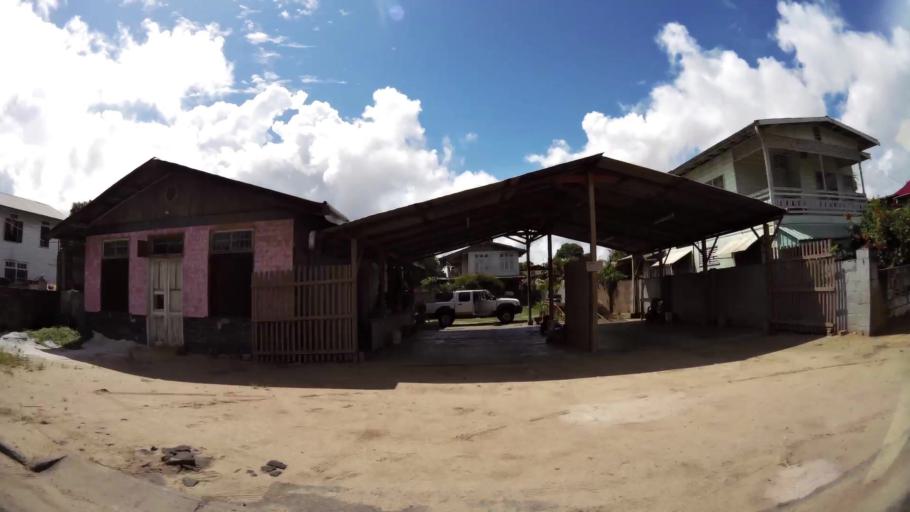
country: SR
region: Paramaribo
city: Paramaribo
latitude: 5.8279
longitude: -55.1755
